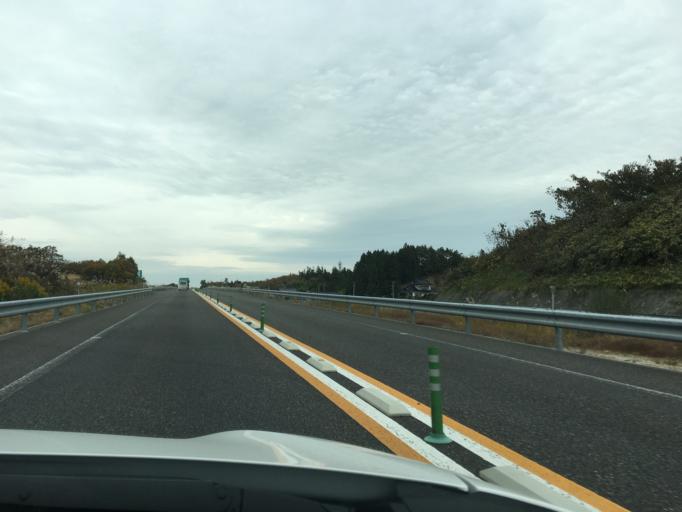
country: JP
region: Fukushima
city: Ishikawa
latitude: 37.2184
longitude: 140.5428
